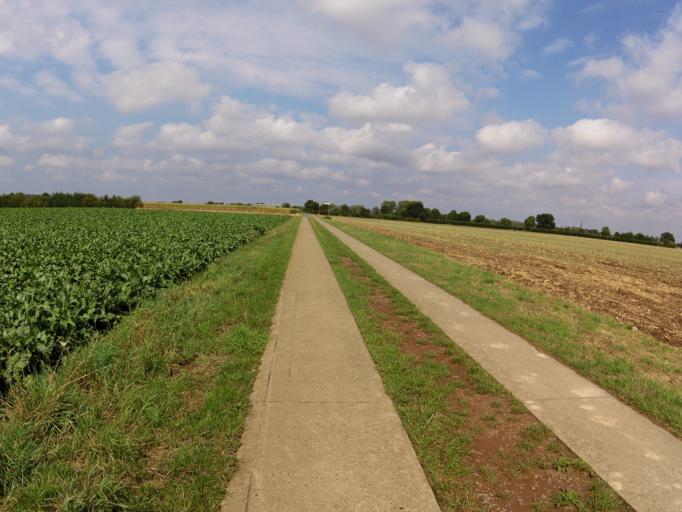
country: DE
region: Lower Saxony
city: Bucken
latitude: 52.7895
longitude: 9.1415
